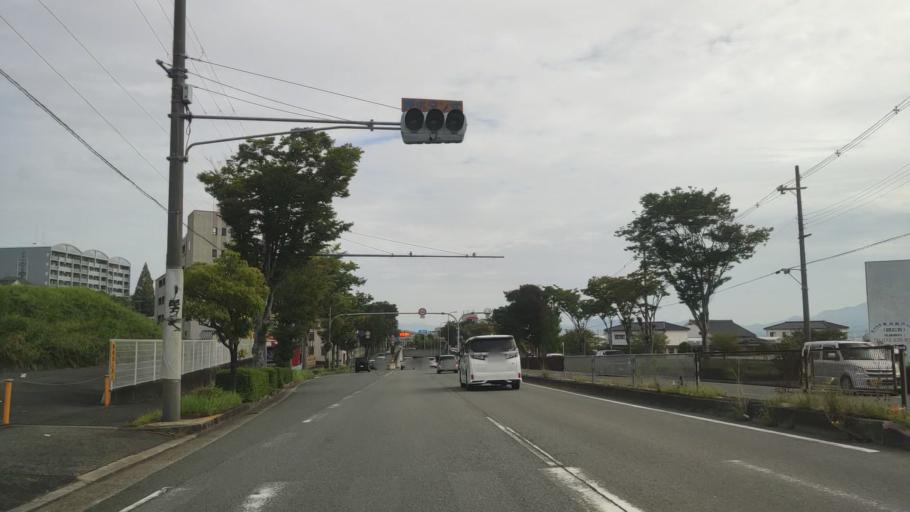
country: JP
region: Osaka
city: Tondabayashicho
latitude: 34.4889
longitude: 135.5827
